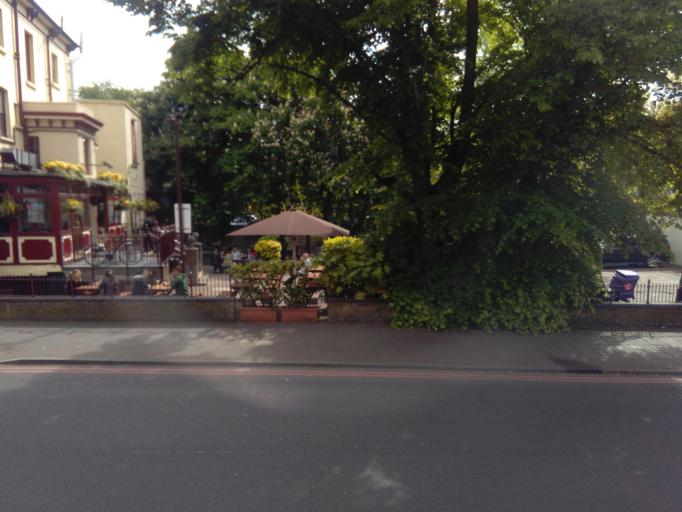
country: GB
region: England
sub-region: Greater London
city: Brixton Hill
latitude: 51.4455
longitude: -0.1251
